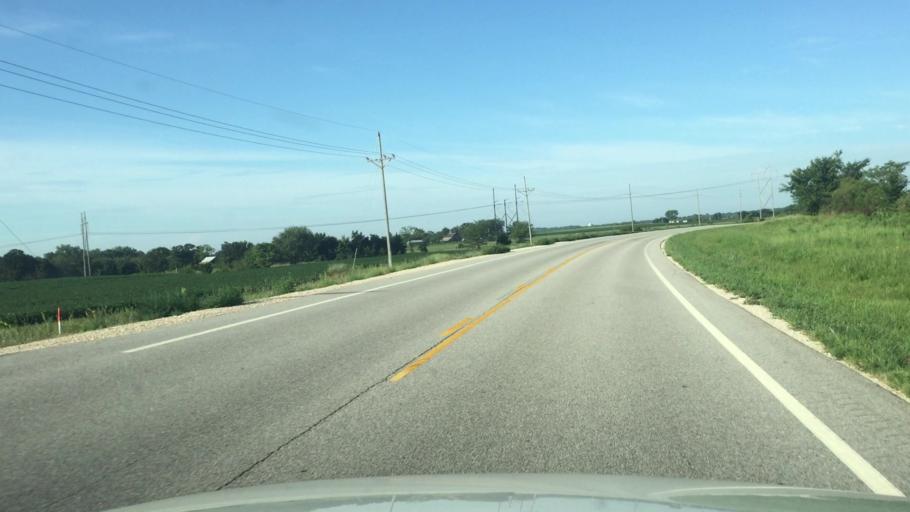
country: US
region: Kansas
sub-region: Anderson County
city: Garnett
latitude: 38.3372
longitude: -95.1670
